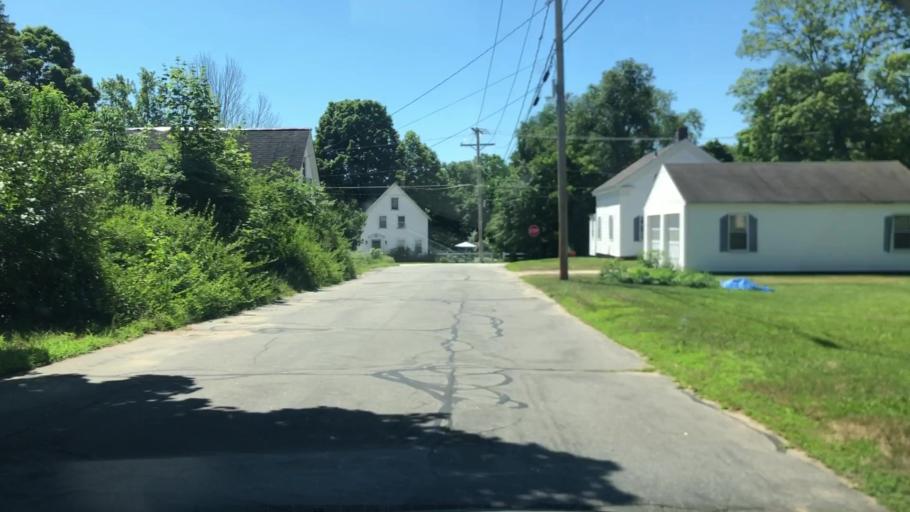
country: US
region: New Hampshire
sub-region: Hillsborough County
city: Milford
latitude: 42.8355
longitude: -71.6371
